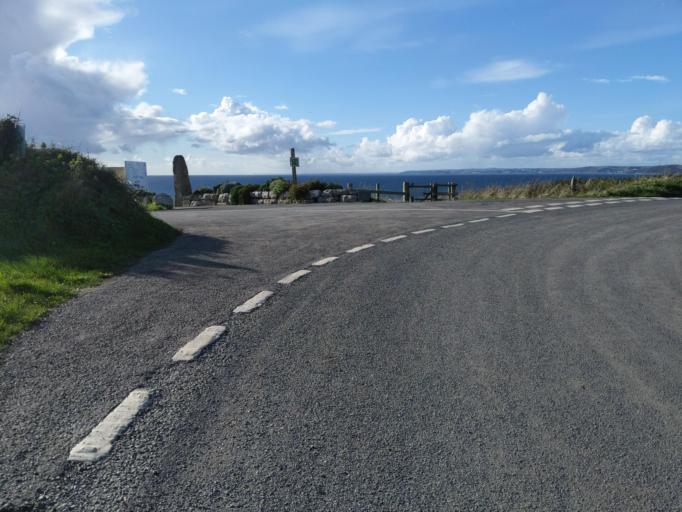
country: GB
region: England
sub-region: Cornwall
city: Millbrook
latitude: 50.3270
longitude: -4.2170
